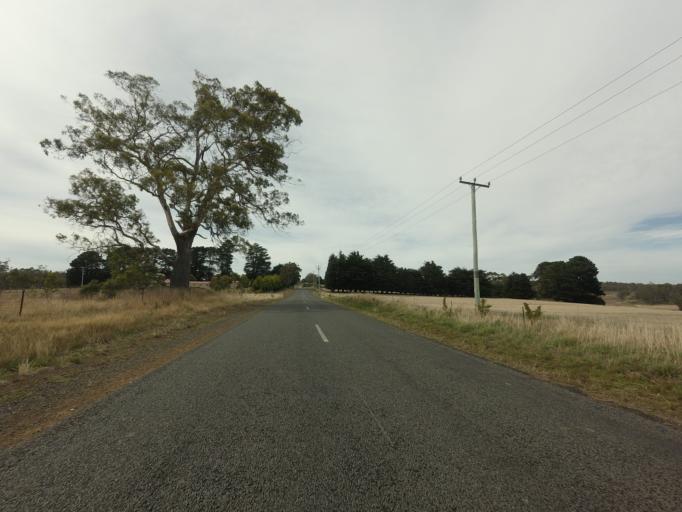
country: AU
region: Tasmania
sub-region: Brighton
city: Bridgewater
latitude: -42.3908
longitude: 147.4293
